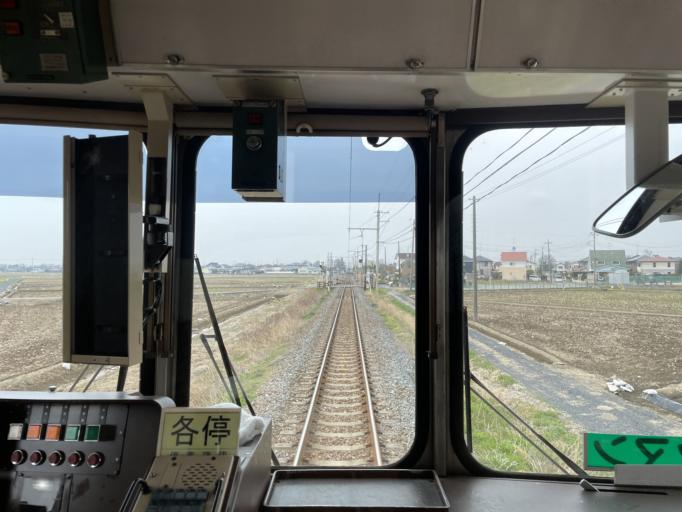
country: JP
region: Saitama
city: Gyoda
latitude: 36.1640
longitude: 139.4922
